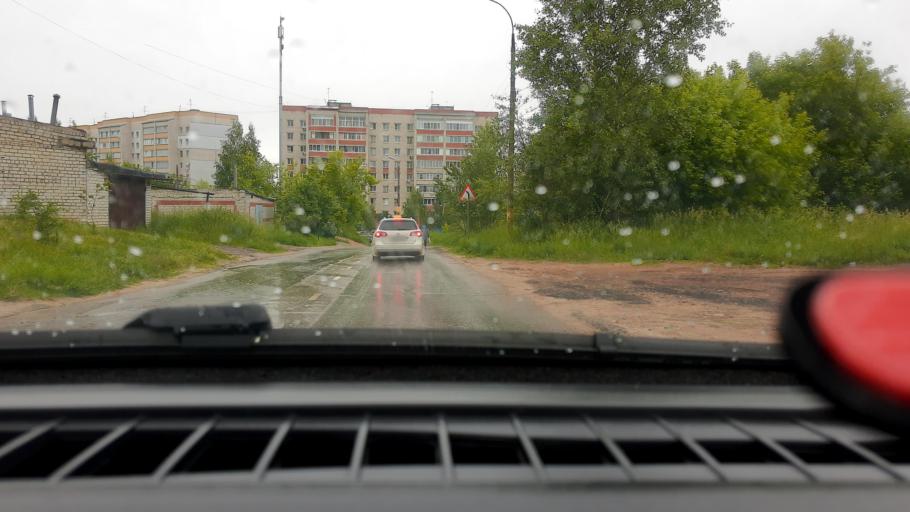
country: RU
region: Nizjnij Novgorod
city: Kstovo
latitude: 56.1491
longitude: 44.1811
